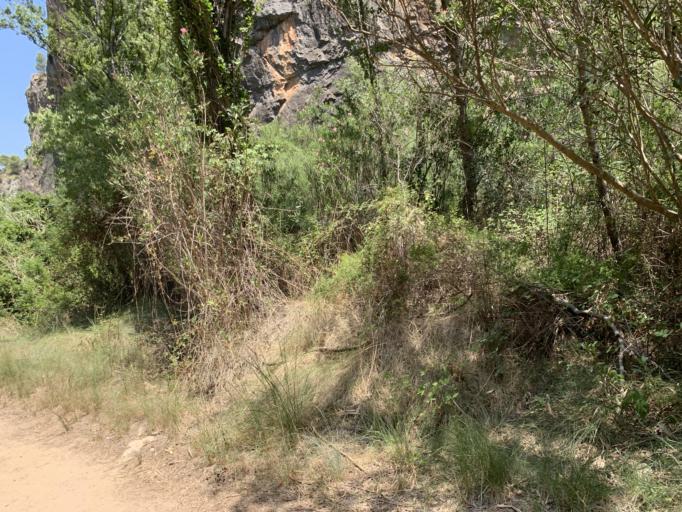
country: ES
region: Valencia
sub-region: Provincia de Valencia
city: Chulilla
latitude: 39.6643
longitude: -0.8928
